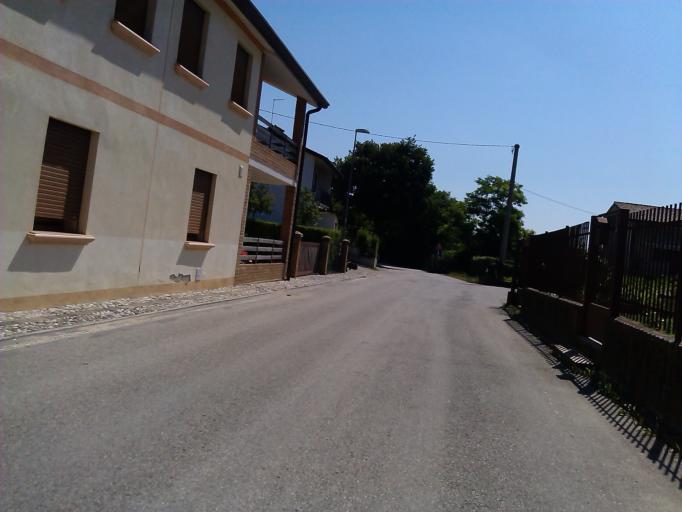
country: IT
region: Veneto
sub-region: Provincia di Treviso
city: Loria Bessica
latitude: 45.7302
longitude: 11.8703
